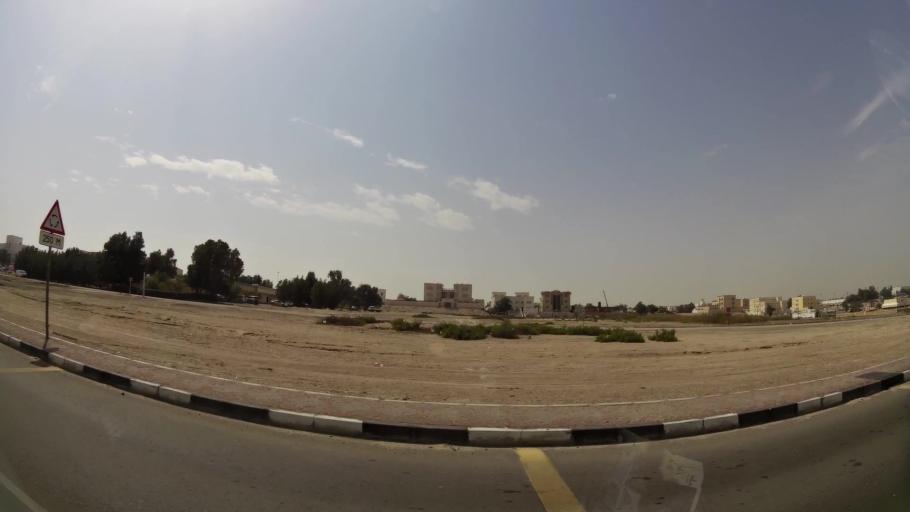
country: AE
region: Abu Dhabi
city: Abu Dhabi
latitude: 24.3031
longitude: 54.6318
